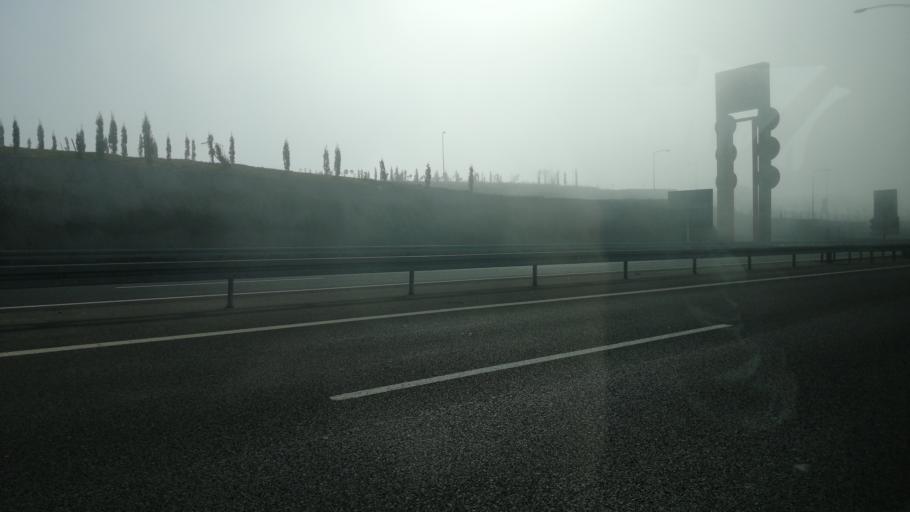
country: TR
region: Kocaeli
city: Tavsanli
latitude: 40.7754
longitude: 29.5183
